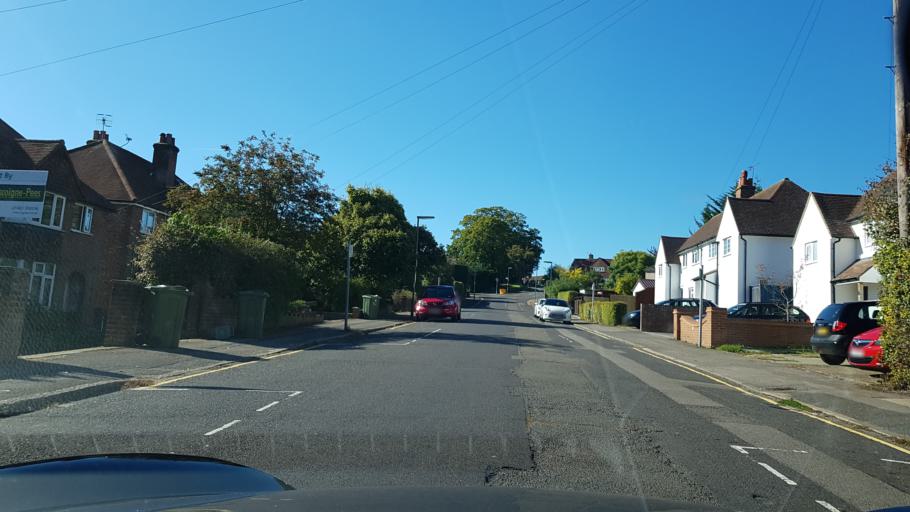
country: GB
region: England
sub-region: Surrey
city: Guildford
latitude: 51.2368
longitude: -0.5915
